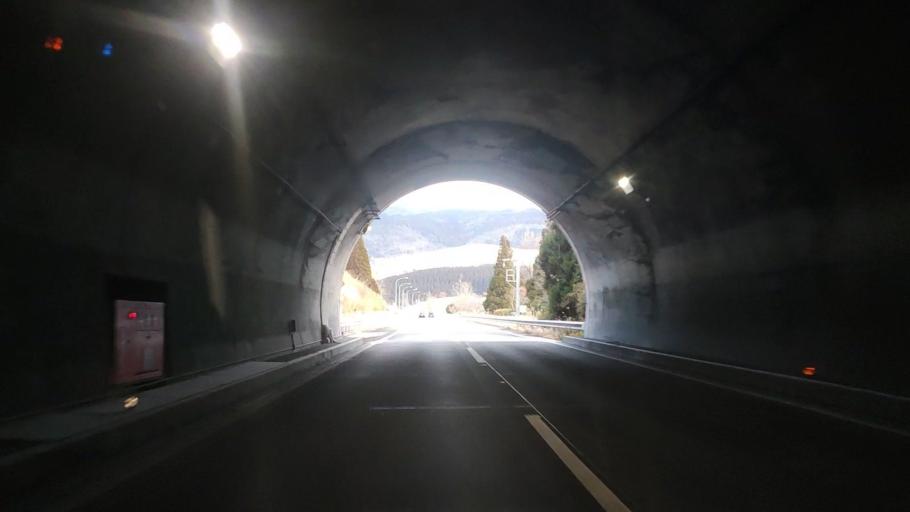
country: JP
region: Oita
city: Beppu
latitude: 33.2789
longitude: 131.3444
